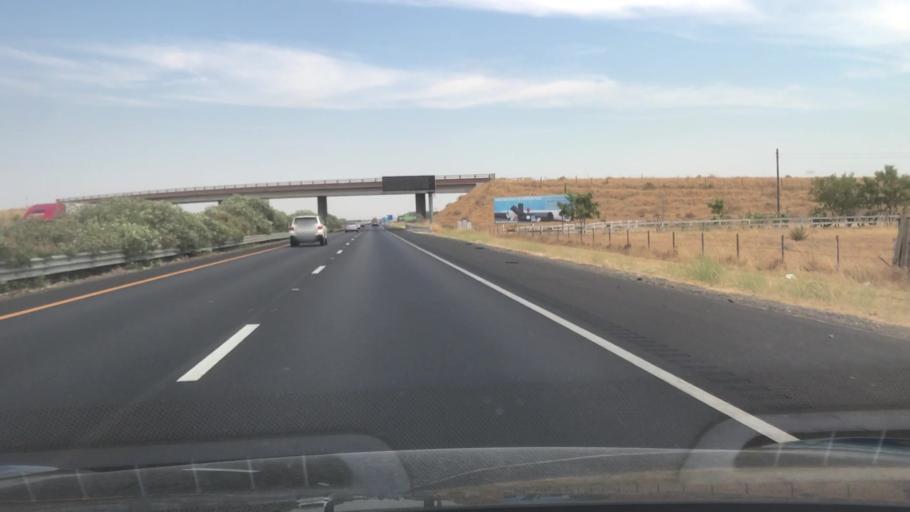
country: US
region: California
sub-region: Fresno County
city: Biola
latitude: 36.8670
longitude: -119.9622
